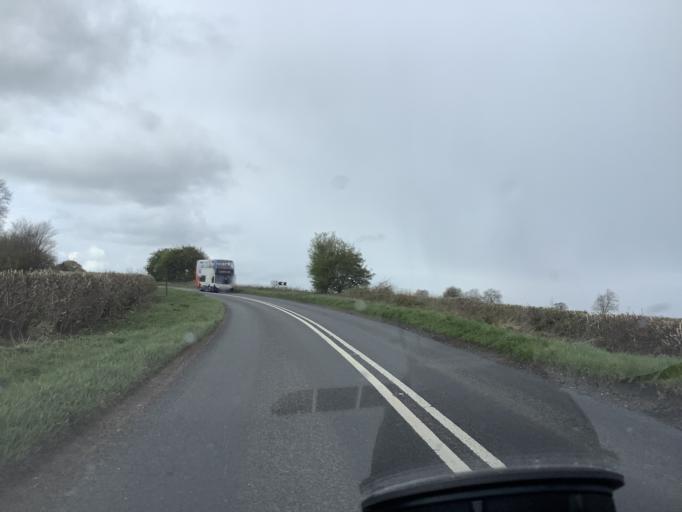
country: GB
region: England
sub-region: Borough of Swindon
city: Wroughton
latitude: 51.5024
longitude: -1.8272
